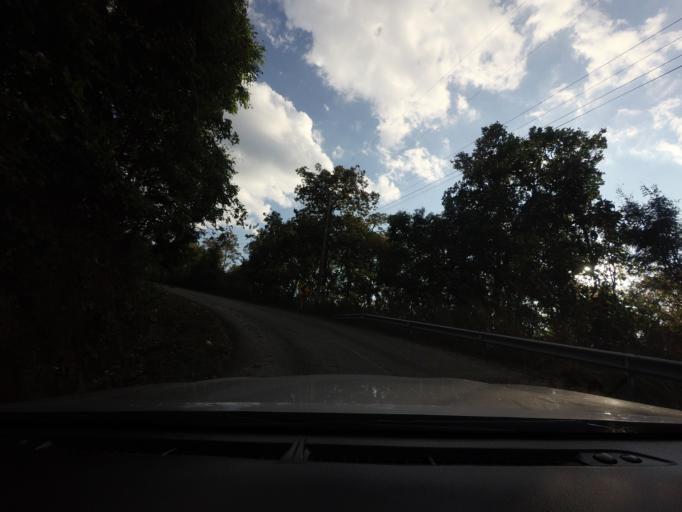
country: TH
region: Chiang Mai
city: Phrao
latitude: 19.5052
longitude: 99.1685
